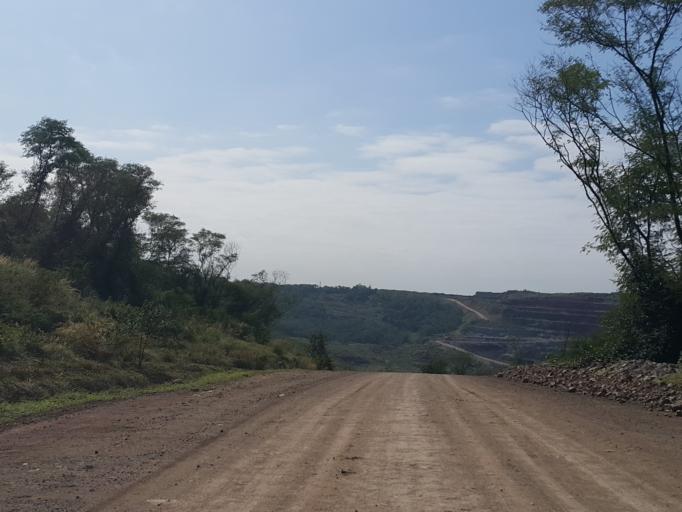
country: TH
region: Lampang
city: Mae Mo
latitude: 18.3277
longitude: 99.7381
